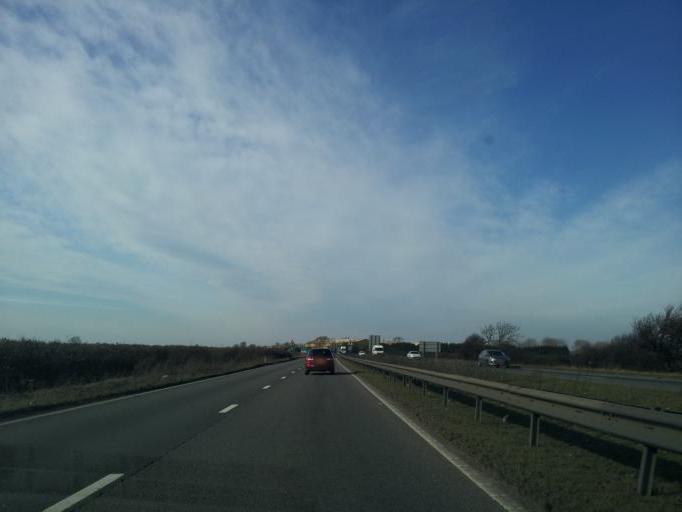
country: GB
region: England
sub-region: Lincolnshire
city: Great Gonerby
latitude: 52.9599
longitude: -0.6889
